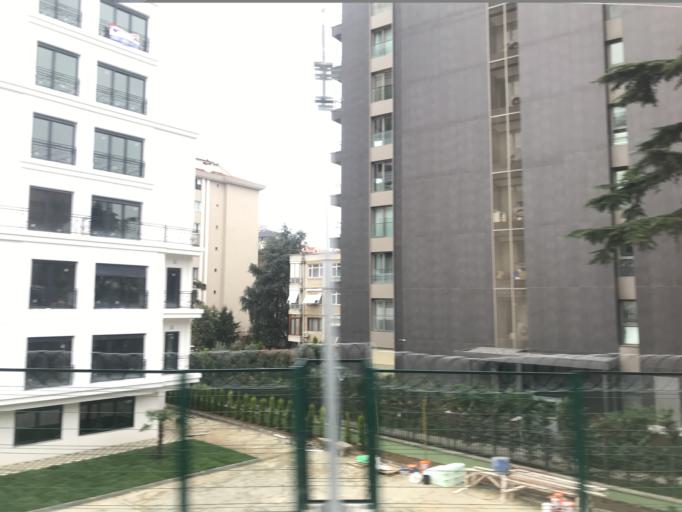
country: TR
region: Istanbul
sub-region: Atasehir
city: Atasehir
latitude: 40.9570
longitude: 29.0907
